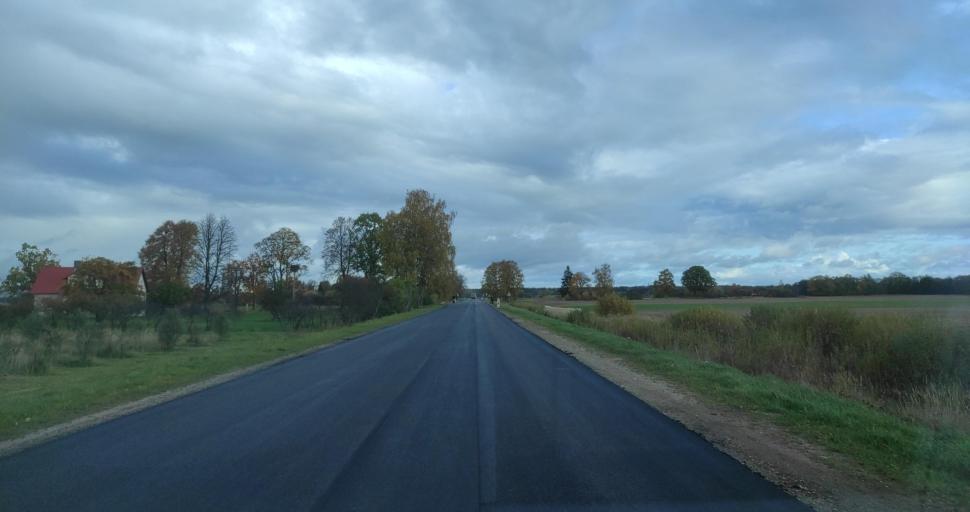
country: LV
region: Skrunda
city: Skrunda
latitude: 56.6867
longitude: 22.0188
